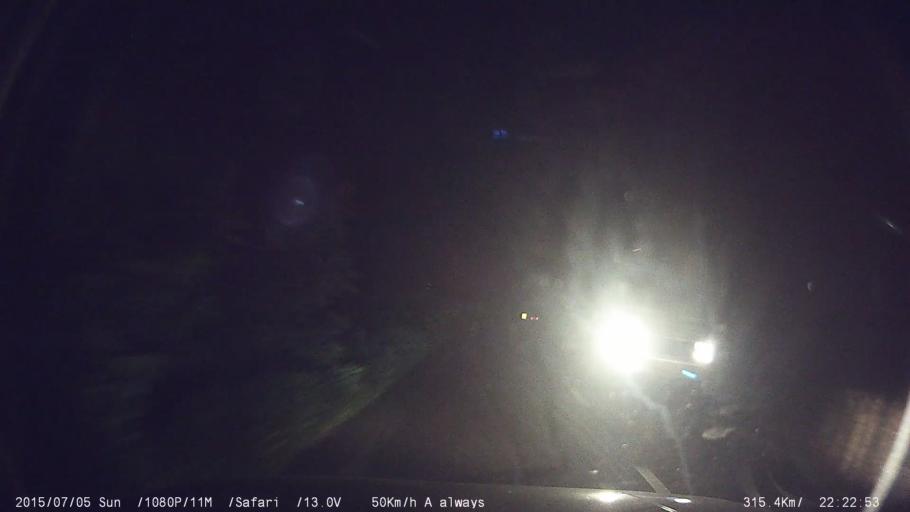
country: IN
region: Kerala
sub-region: Palakkad district
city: Palakkad
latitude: 10.8253
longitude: 76.5928
